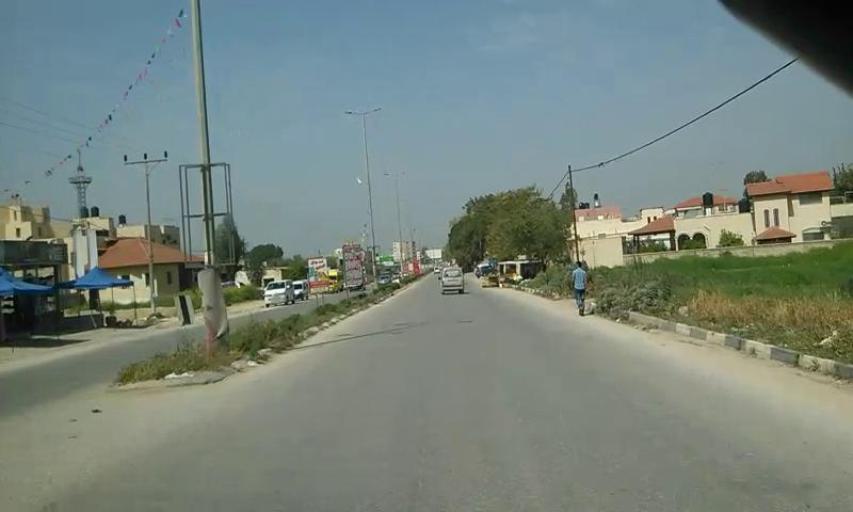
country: PS
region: West Bank
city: Janin
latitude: 32.4738
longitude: 35.3020
